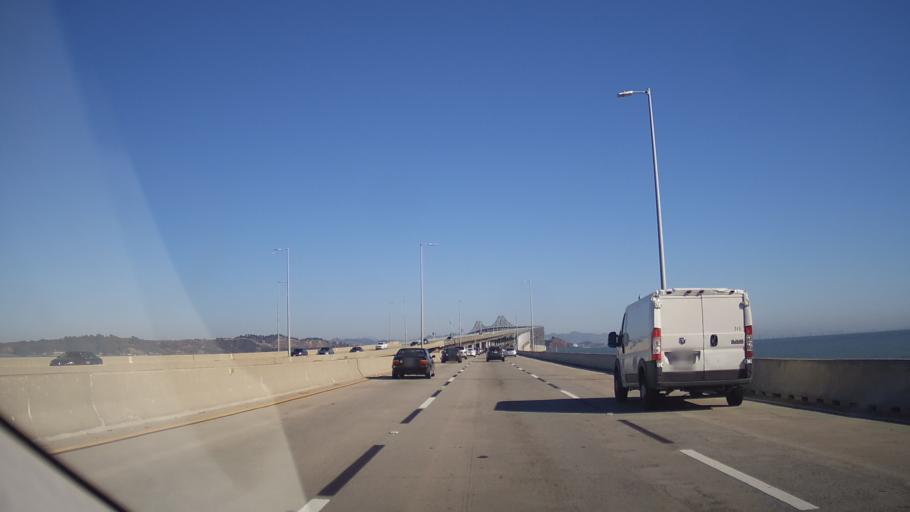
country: US
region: California
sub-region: Marin County
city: Strawberry
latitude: 37.9412
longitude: -122.4710
